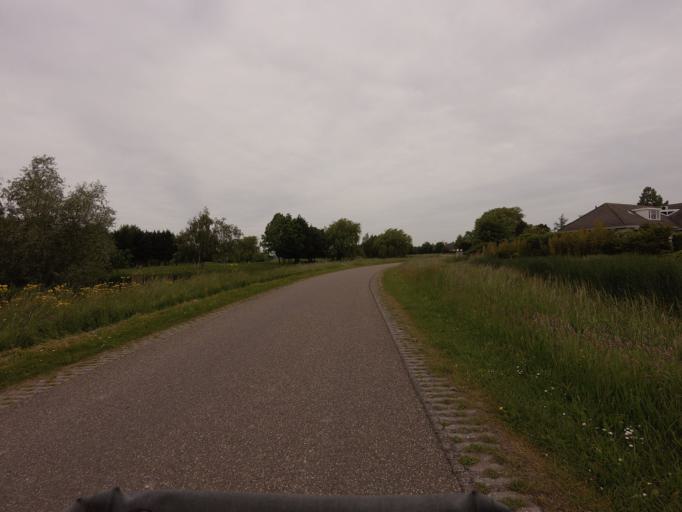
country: NL
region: North Holland
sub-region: Gemeente Medemblik
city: Medemblik
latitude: 52.7473
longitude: 5.1091
